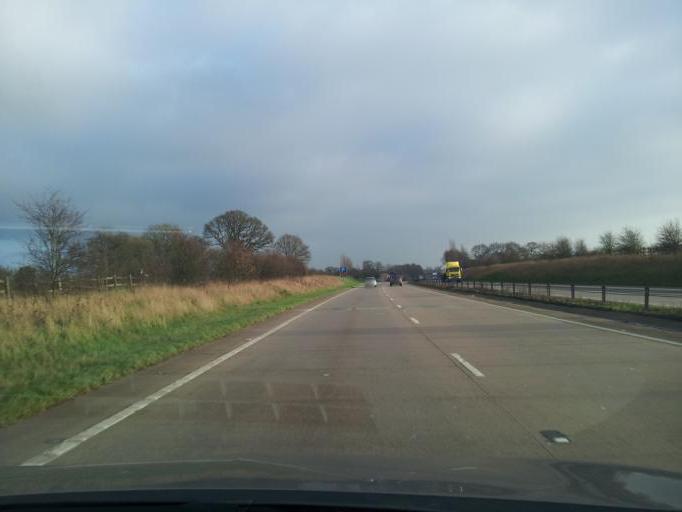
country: GB
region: England
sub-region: Staffordshire
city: Uttoxeter
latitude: 52.9008
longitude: -1.7971
